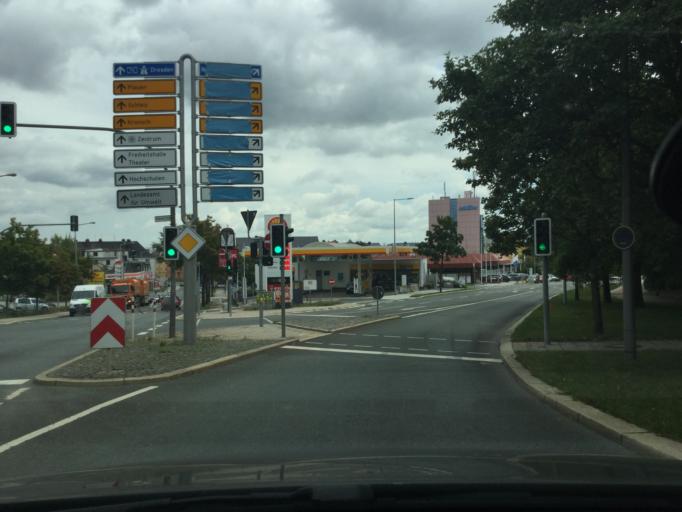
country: DE
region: Bavaria
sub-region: Upper Franconia
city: Hof
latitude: 50.3170
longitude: 11.8971
